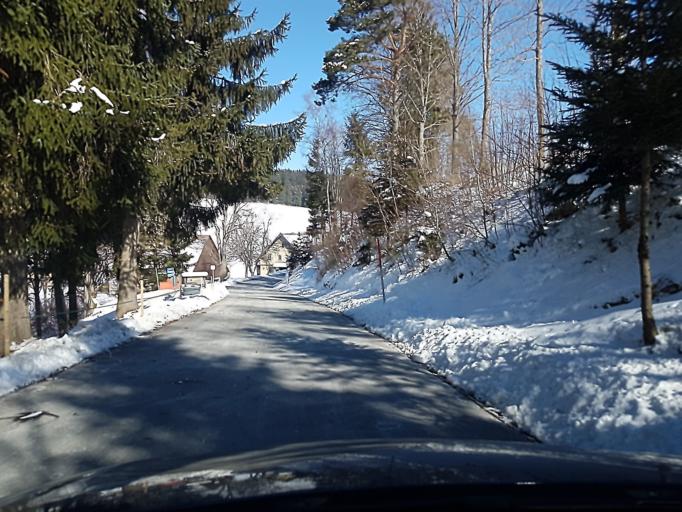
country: DE
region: Baden-Wuerttemberg
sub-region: Freiburg Region
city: Sankt Georgen im Schwarzwald
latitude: 48.1576
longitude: 8.2963
